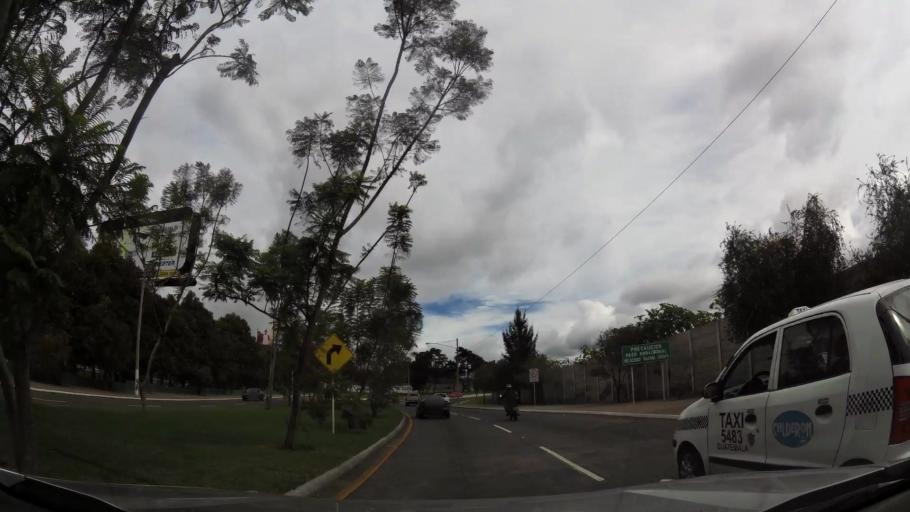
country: GT
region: Guatemala
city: Santa Catarina Pinula
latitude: 14.5940
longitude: -90.5276
